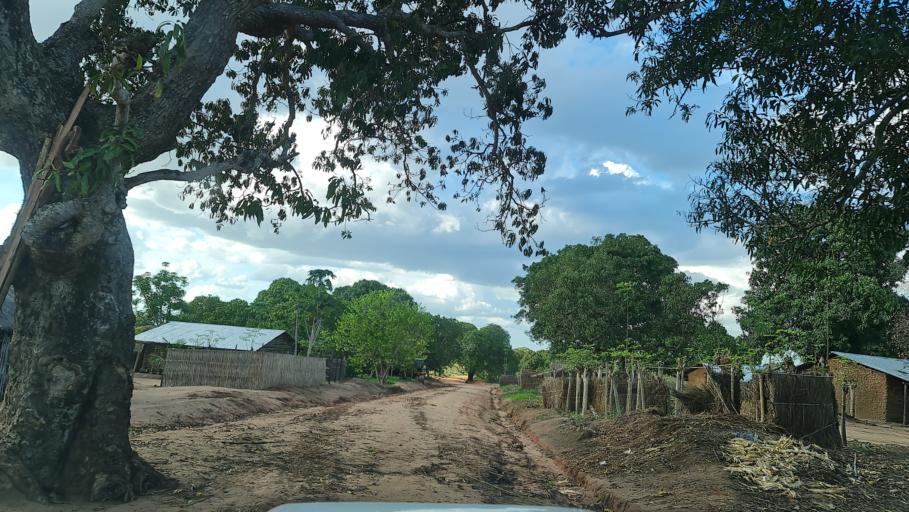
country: MZ
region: Cabo Delgado
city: Pemba
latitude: -13.5544
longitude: 40.1037
